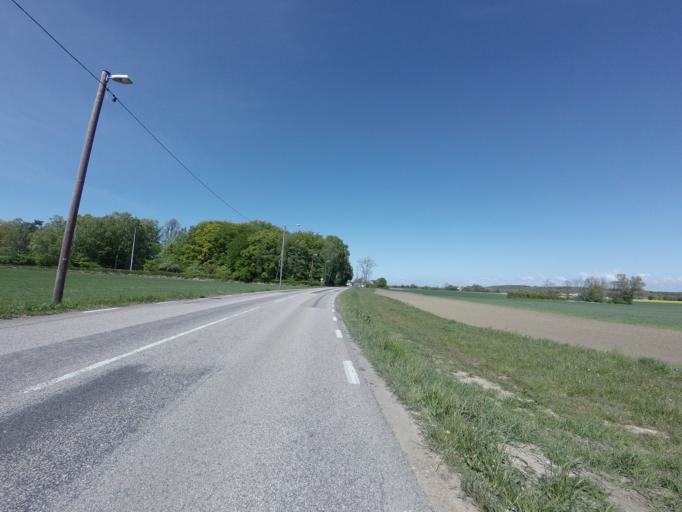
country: SE
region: Skane
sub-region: Helsingborg
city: Odakra
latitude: 56.1492
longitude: 12.6782
